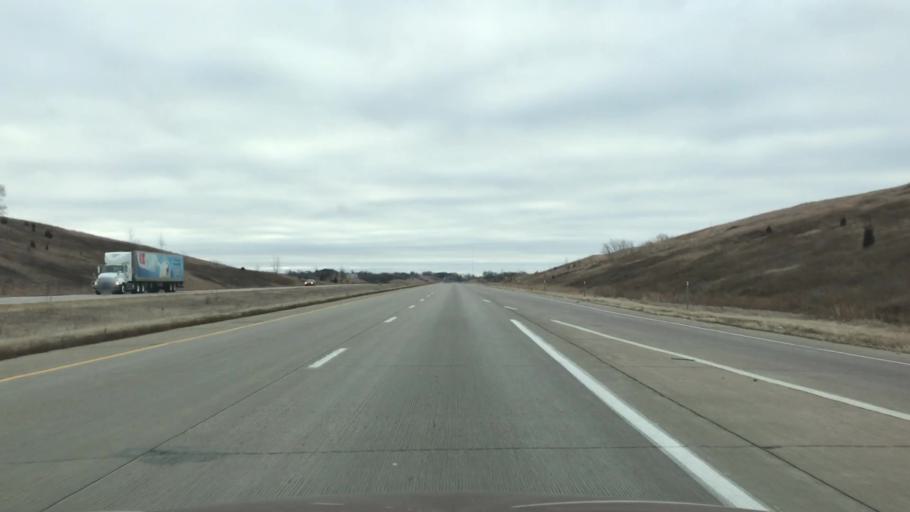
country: US
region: Iowa
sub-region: Woodbury County
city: Sioux City
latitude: 42.5151
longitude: -96.3360
